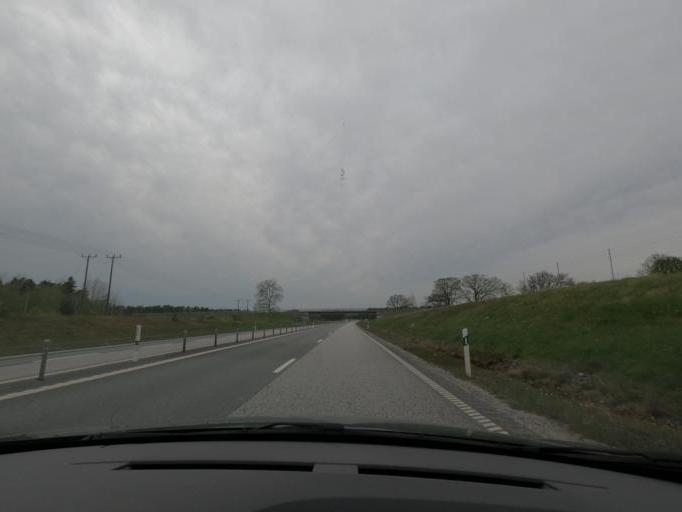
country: SE
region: Joenkoeping
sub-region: Gislaveds Kommun
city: Gislaved
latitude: 57.3020
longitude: 13.5823
